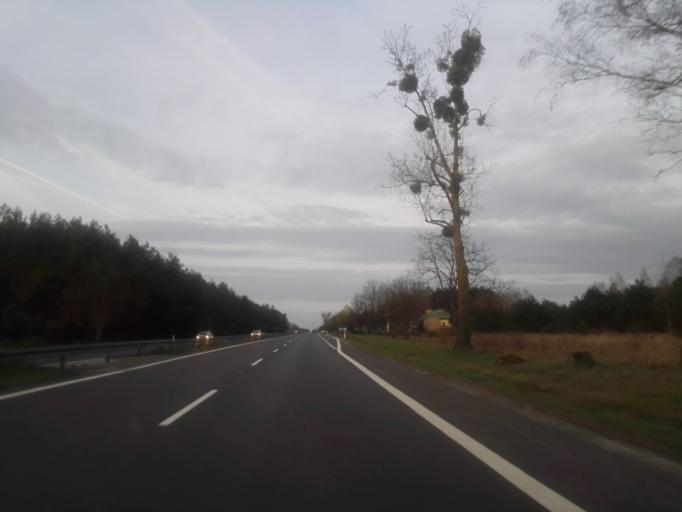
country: PL
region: Lodz Voivodeship
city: Zabia Wola
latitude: 52.0451
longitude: 20.7055
